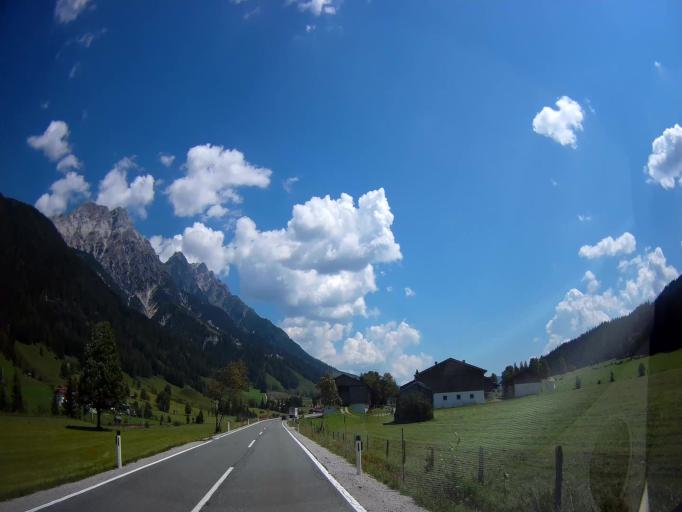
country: AT
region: Tyrol
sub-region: Politischer Bezirk Kitzbuhel
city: Hochfilzen
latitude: 47.4533
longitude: 12.6629
